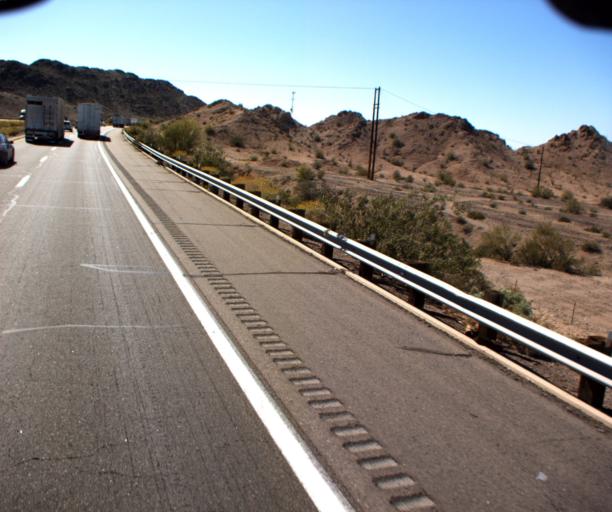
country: US
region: Arizona
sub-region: Yuma County
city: Wellton
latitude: 32.7276
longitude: -113.7386
